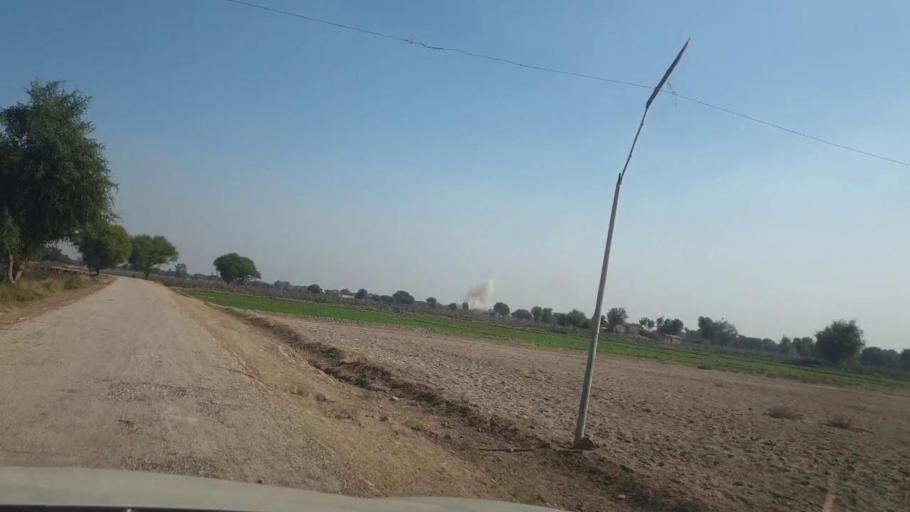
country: PK
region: Sindh
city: Bhan
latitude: 26.5787
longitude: 67.6971
